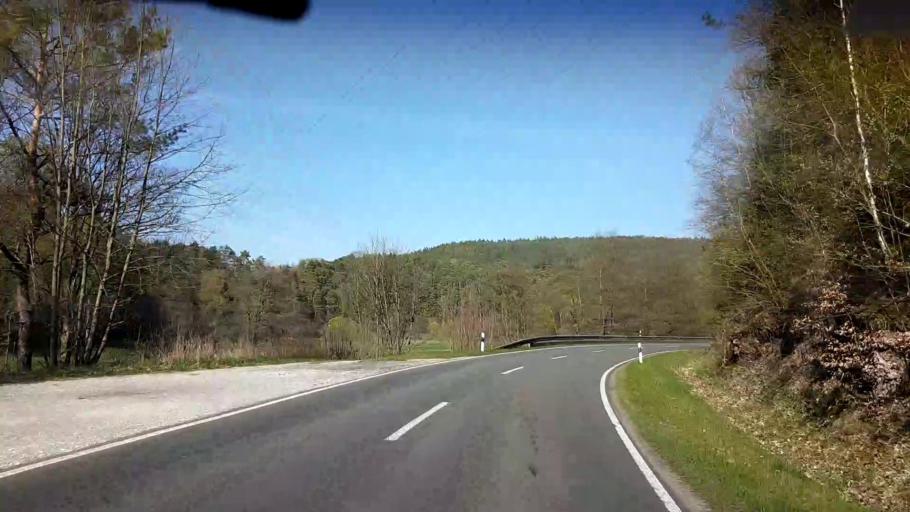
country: DE
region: Bavaria
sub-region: Upper Franconia
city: Plankenfels
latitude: 49.8743
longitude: 11.3377
